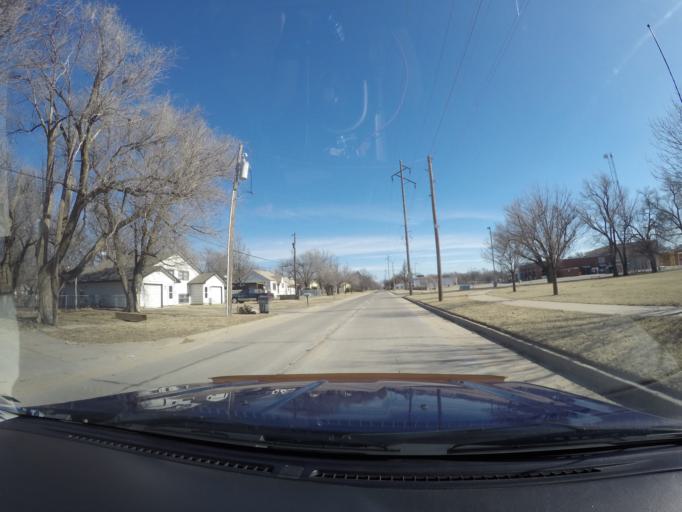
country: US
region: Kansas
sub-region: Sedgwick County
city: Wichita
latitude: 37.6874
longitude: -97.4013
